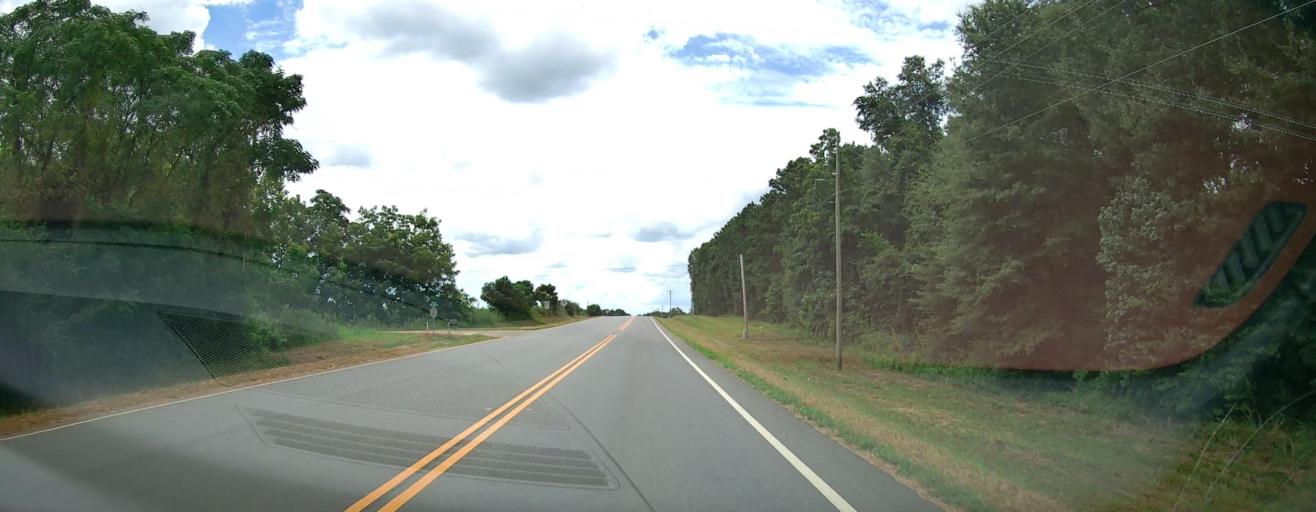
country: US
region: Georgia
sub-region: Macon County
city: Montezuma
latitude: 32.2918
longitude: -83.9267
